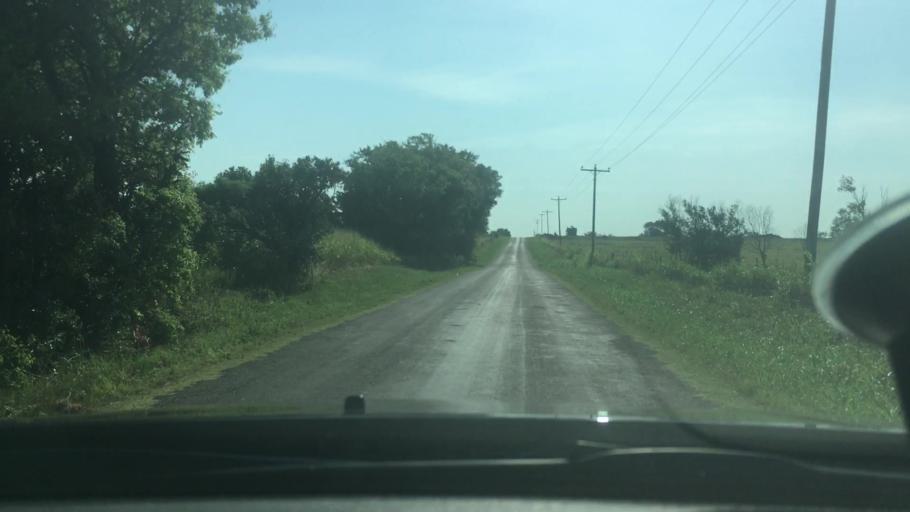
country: US
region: Oklahoma
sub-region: Garvin County
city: Maysville
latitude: 34.6520
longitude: -97.3772
